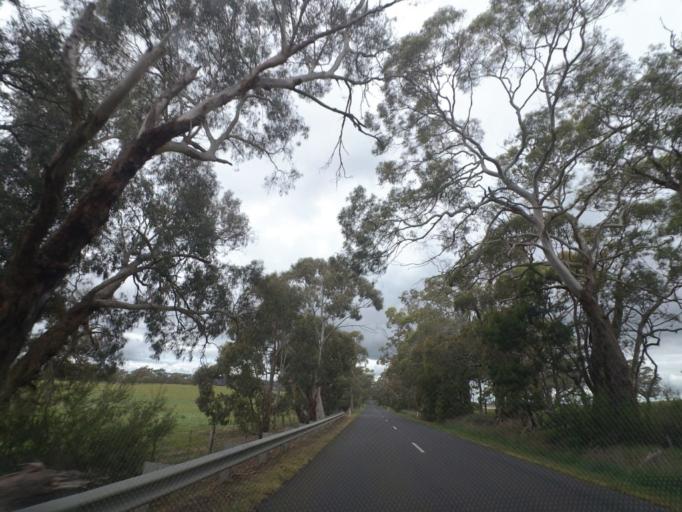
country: AU
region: Victoria
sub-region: Hume
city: Sunbury
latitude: -37.3587
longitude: 144.8211
